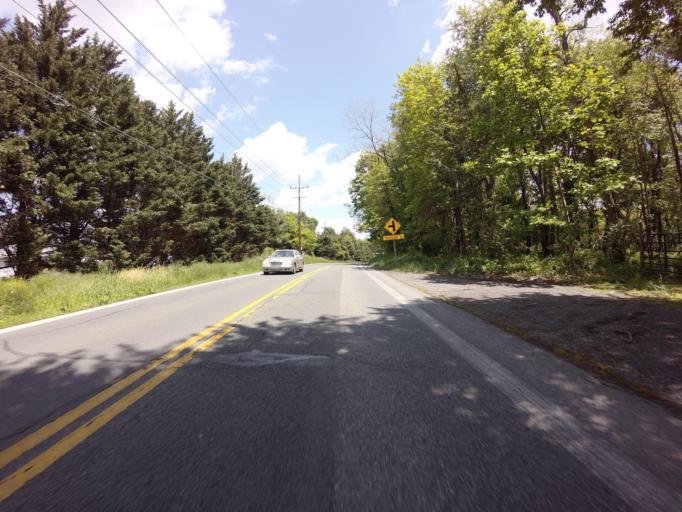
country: US
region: Maryland
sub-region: Montgomery County
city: Damascus
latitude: 39.3404
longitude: -77.2401
